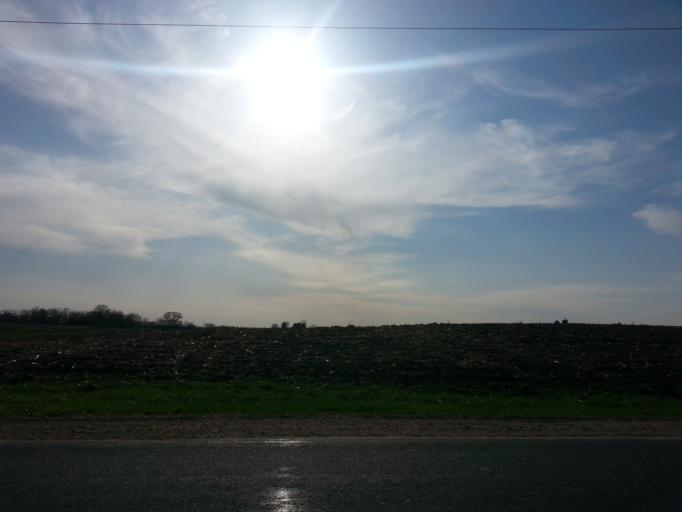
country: US
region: Wisconsin
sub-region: Pierce County
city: Ellsworth
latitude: 44.6825
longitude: -92.6090
